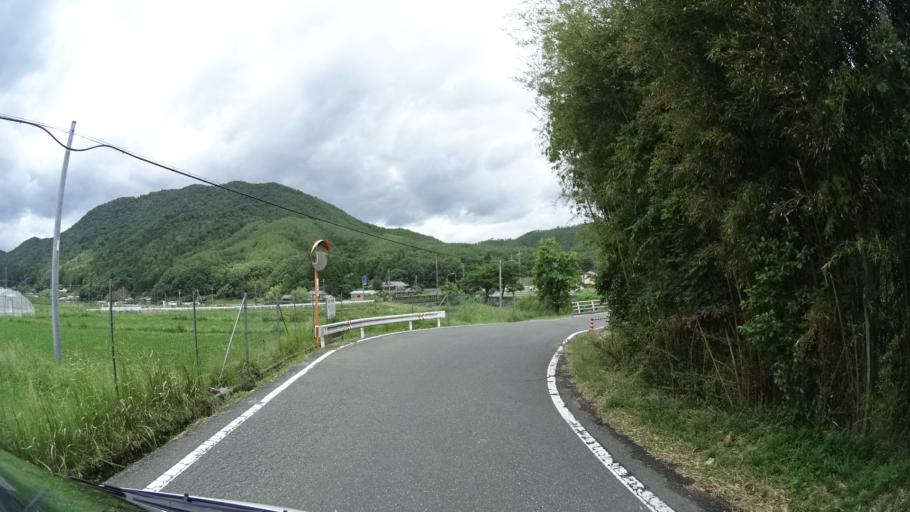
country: JP
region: Kyoto
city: Kameoka
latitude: 35.0481
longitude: 135.4143
